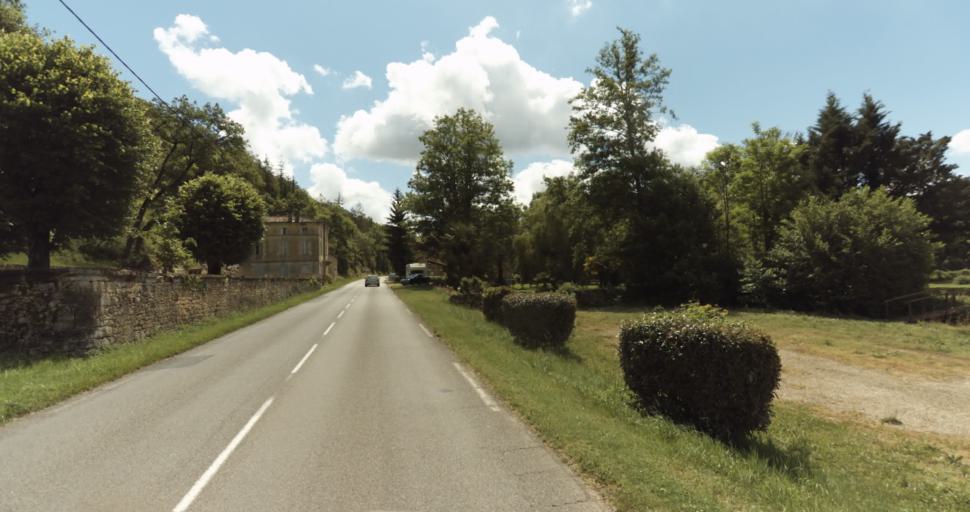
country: FR
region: Aquitaine
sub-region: Departement de la Dordogne
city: Lalinde
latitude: 44.8024
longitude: 0.7352
